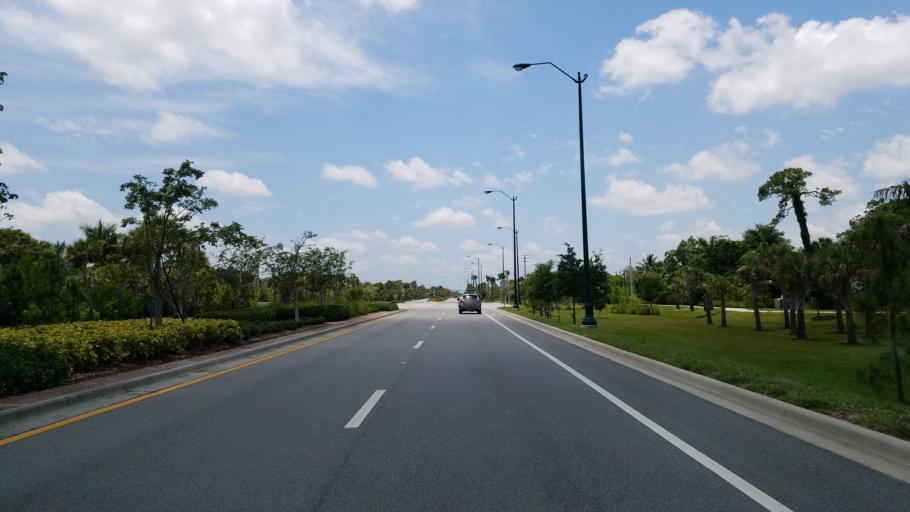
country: US
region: Florida
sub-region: Martin County
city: Palm City
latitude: 27.1612
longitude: -80.2627
